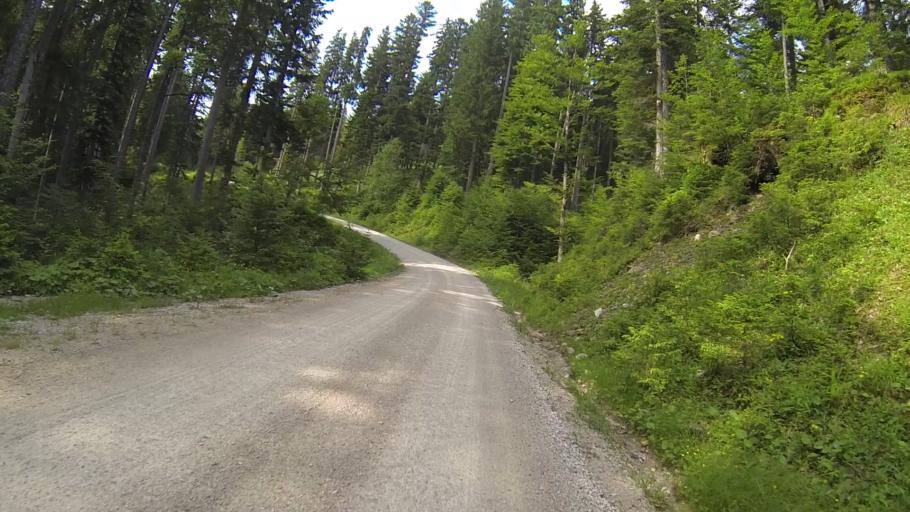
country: AT
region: Tyrol
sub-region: Politischer Bezirk Reutte
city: Jungholz
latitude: 47.5750
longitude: 10.4724
